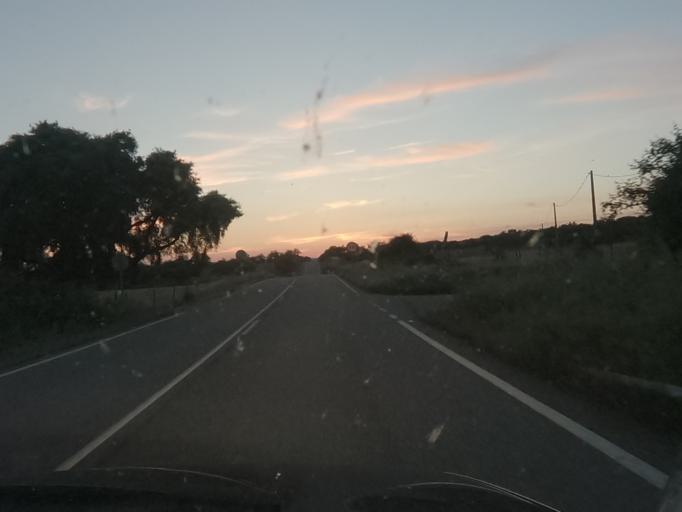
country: ES
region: Extremadura
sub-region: Provincia de Caceres
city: Piedras Albas
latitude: 39.7821
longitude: -6.9325
